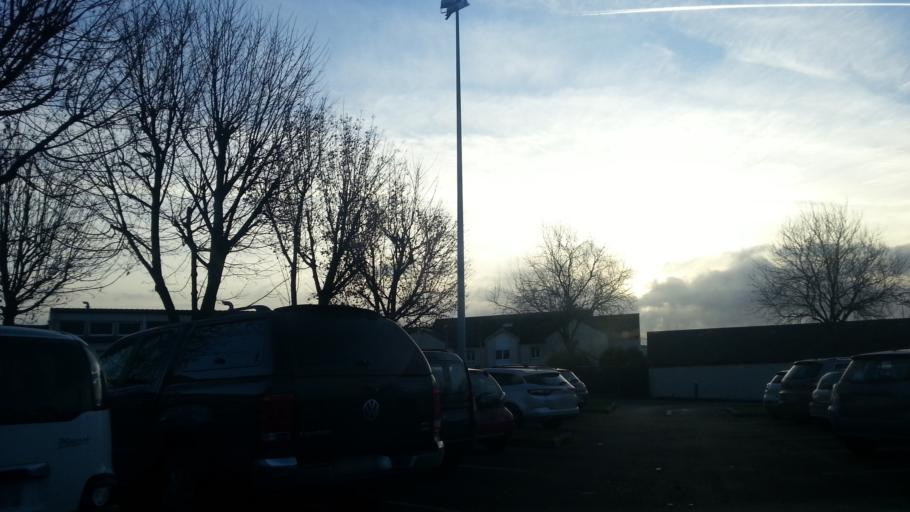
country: FR
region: Picardie
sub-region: Departement de l'Oise
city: Montataire
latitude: 49.2604
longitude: 2.4377
